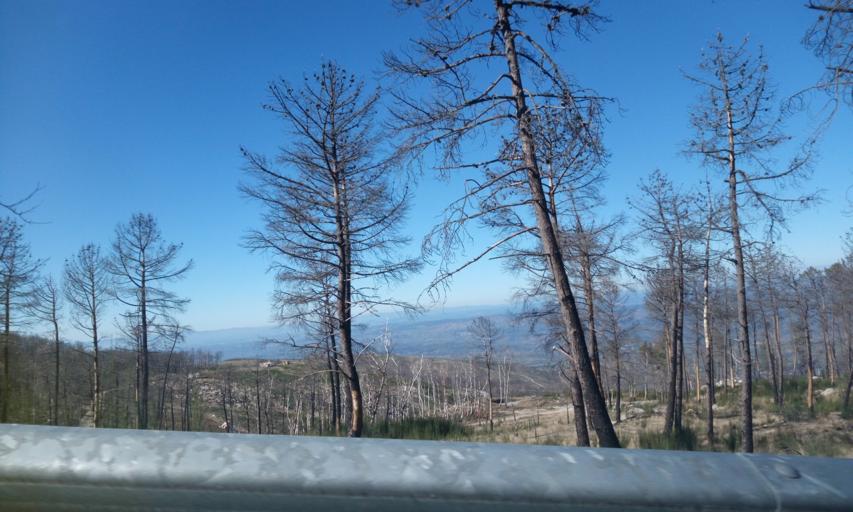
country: PT
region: Guarda
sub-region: Manteigas
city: Manteigas
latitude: 40.4914
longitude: -7.5222
